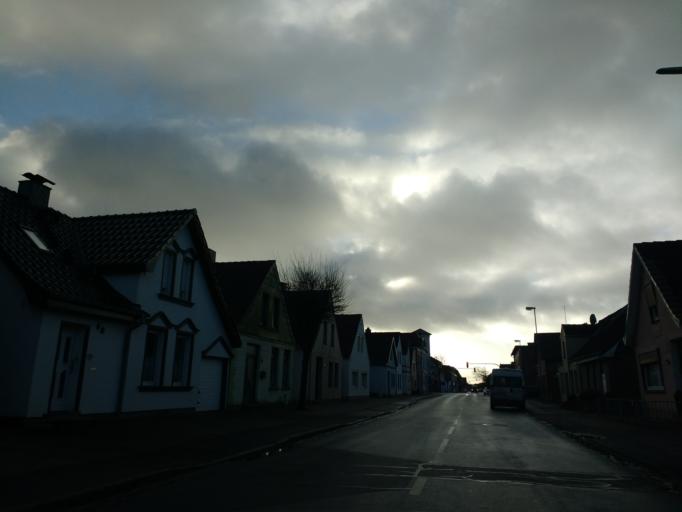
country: DE
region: Schleswig-Holstein
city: Brunsbuttel
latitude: 53.8988
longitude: 9.1297
